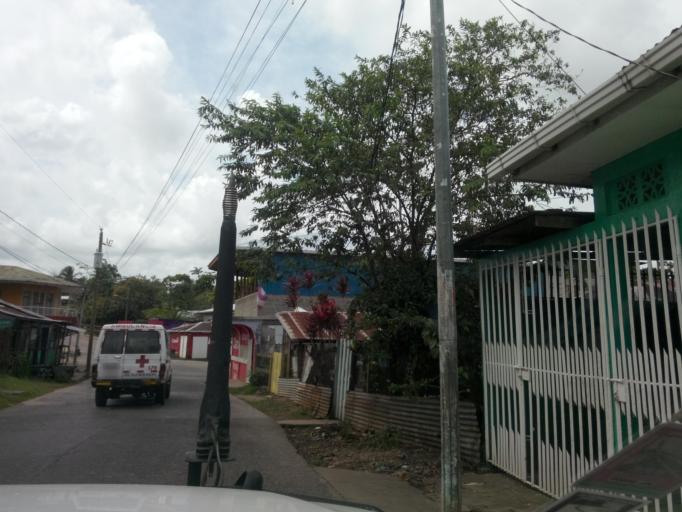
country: NI
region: Atlantico Sur
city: Bluefields
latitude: 12.0126
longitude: -83.7715
